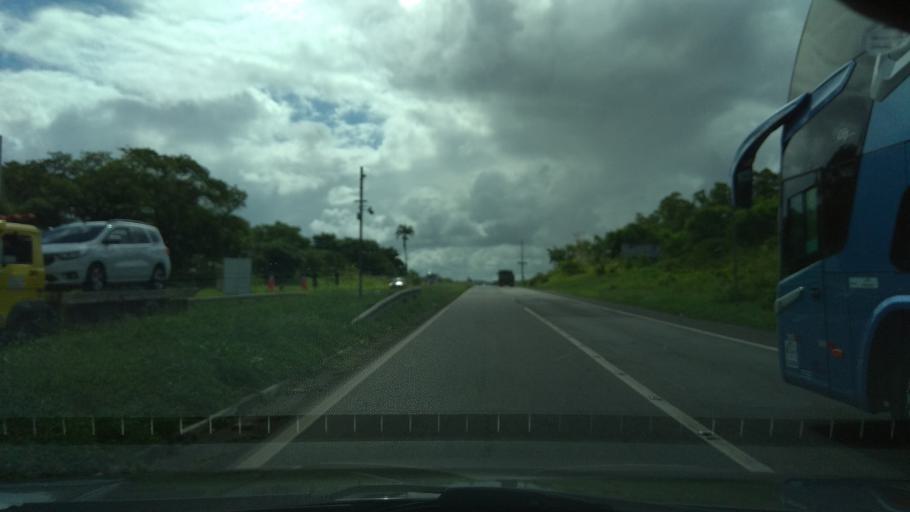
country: BR
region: Bahia
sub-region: Simoes Filho
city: Simoes Filho
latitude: -12.7729
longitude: -38.4193
